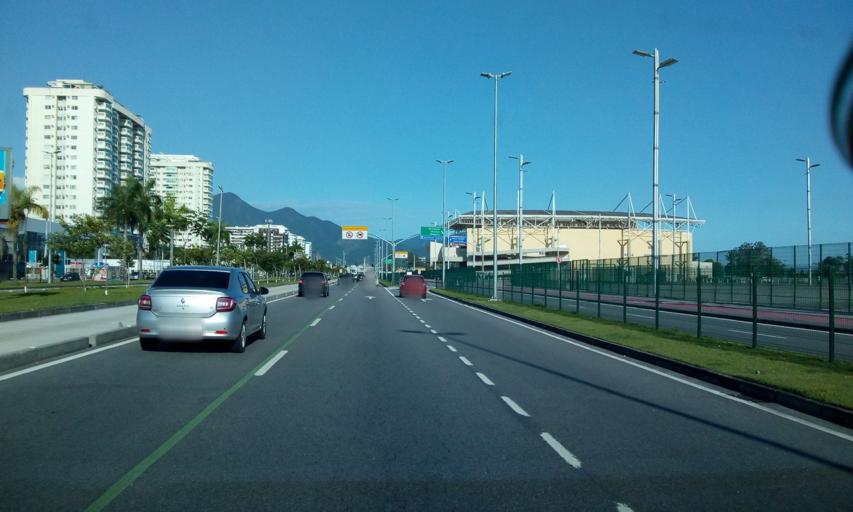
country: BR
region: Rio de Janeiro
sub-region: Nilopolis
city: Nilopolis
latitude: -22.9733
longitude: -43.3917
